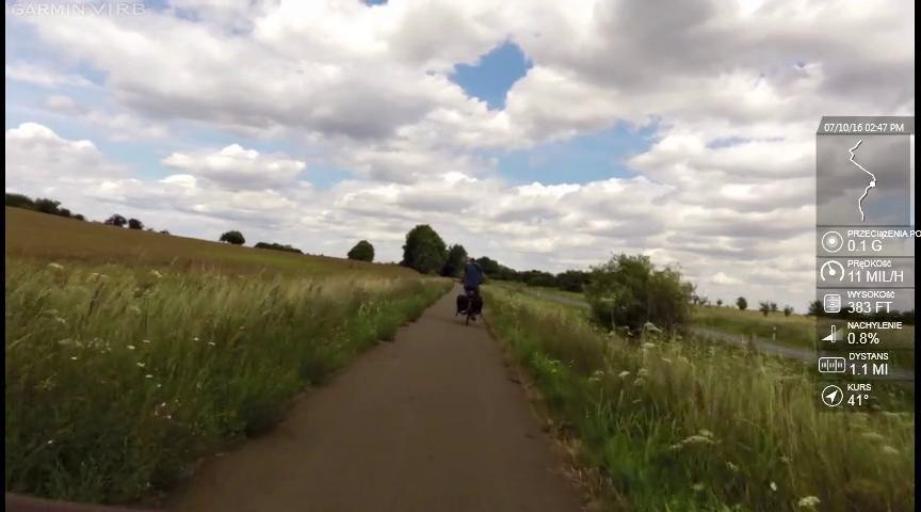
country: PL
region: West Pomeranian Voivodeship
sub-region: Powiat gryfinski
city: Banie
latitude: 53.0901
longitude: 14.6464
